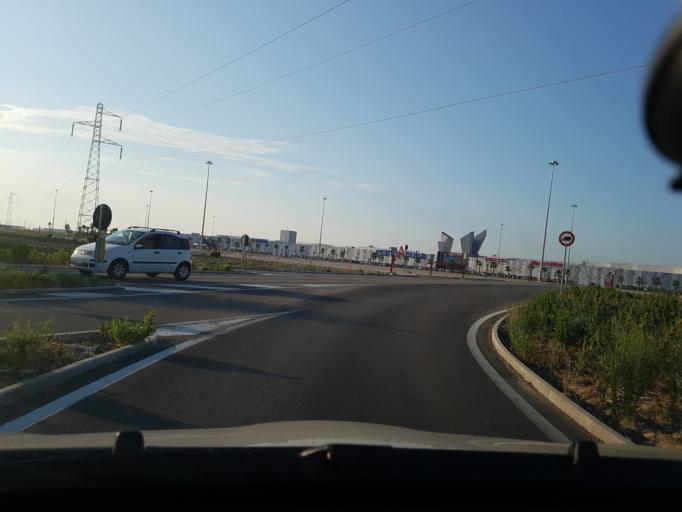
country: IT
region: Apulia
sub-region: Provincia di Foggia
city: Carapelle
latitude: 41.4126
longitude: 15.6513
